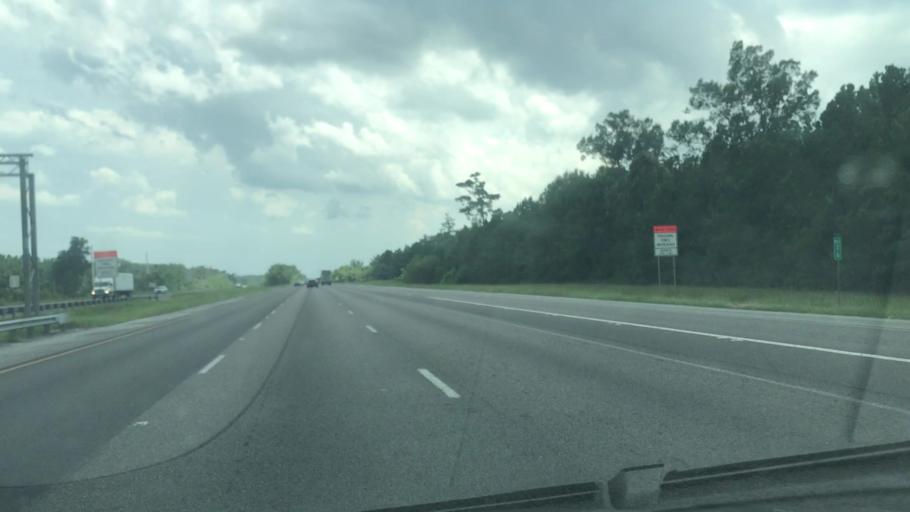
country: US
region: Georgia
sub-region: Liberty County
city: Midway
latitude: 31.7726
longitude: -81.3800
